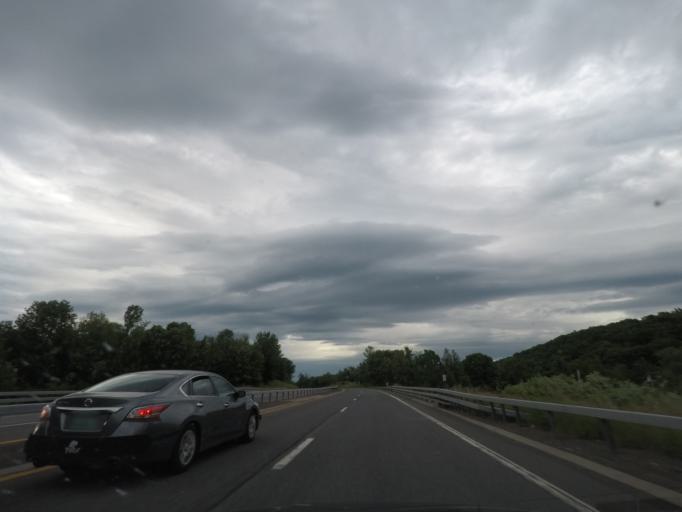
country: US
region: New York
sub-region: Dutchess County
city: Pine Plains
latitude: 42.0733
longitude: -73.7173
